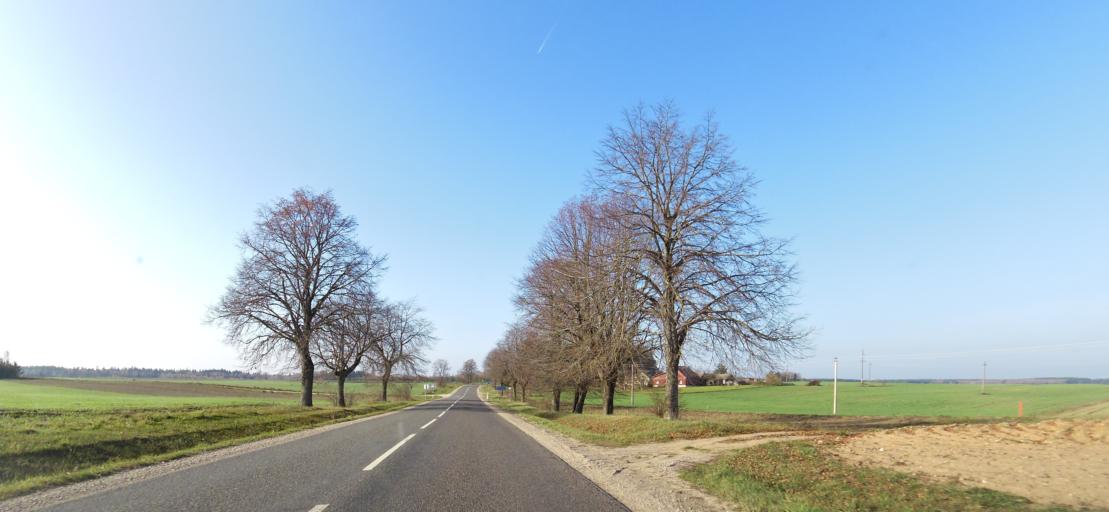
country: LT
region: Vilnius County
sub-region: Trakai
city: Rudiskes
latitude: 54.5112
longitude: 24.7970
